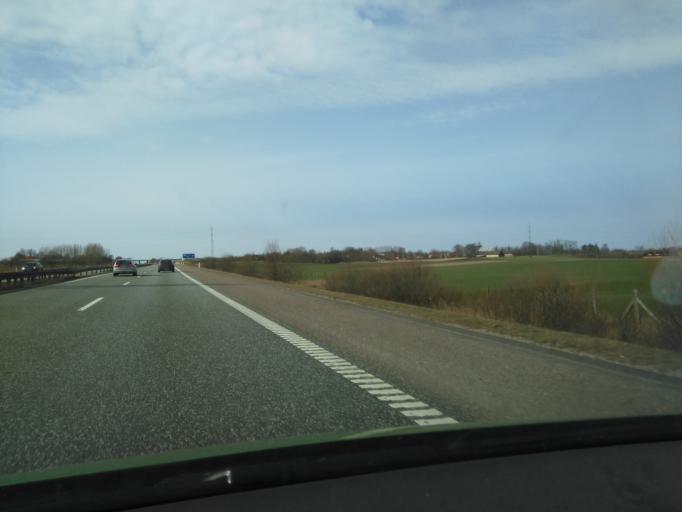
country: DK
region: Central Jutland
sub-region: Arhus Kommune
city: Framlev
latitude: 56.1530
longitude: 10.0223
